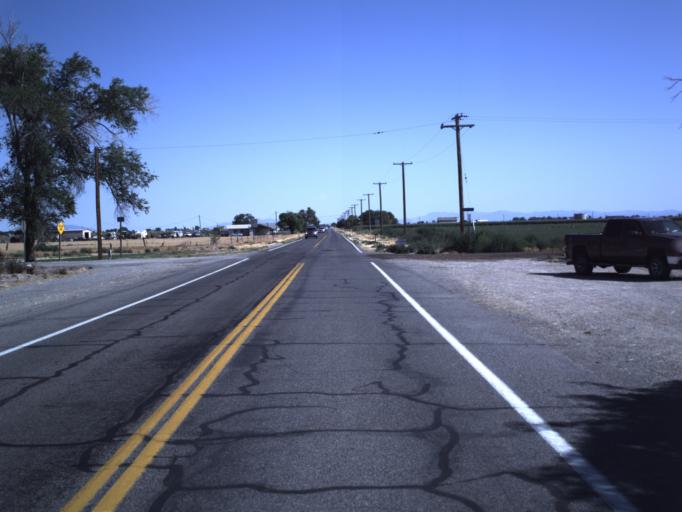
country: US
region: Utah
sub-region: Millard County
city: Delta
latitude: 39.2938
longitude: -112.6526
